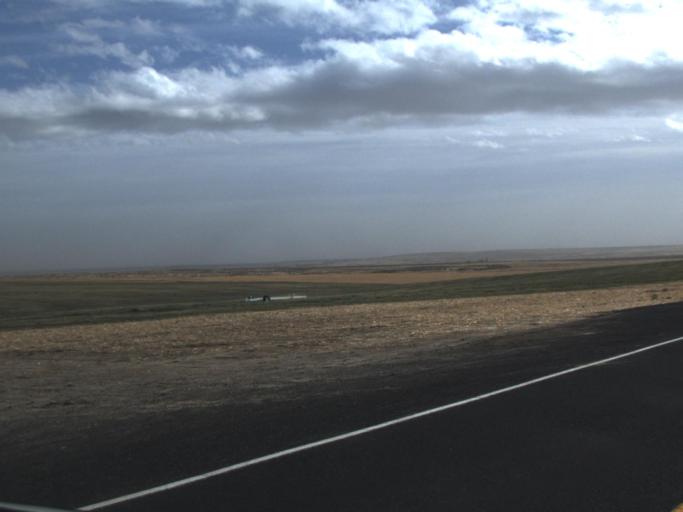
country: US
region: Washington
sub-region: Okanogan County
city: Coulee Dam
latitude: 47.5863
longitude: -118.7861
